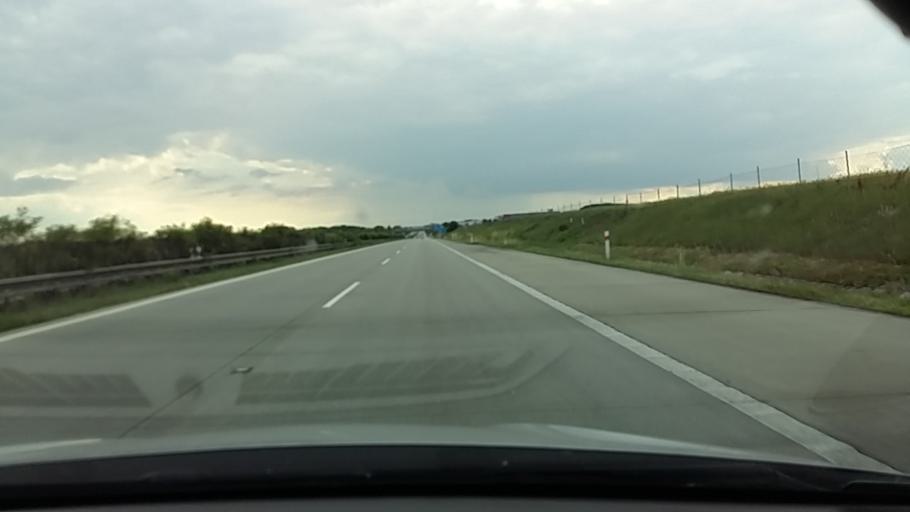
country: CZ
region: Plzensky
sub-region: Okres Plzen-Sever
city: Tlucna
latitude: 49.7085
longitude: 13.2374
